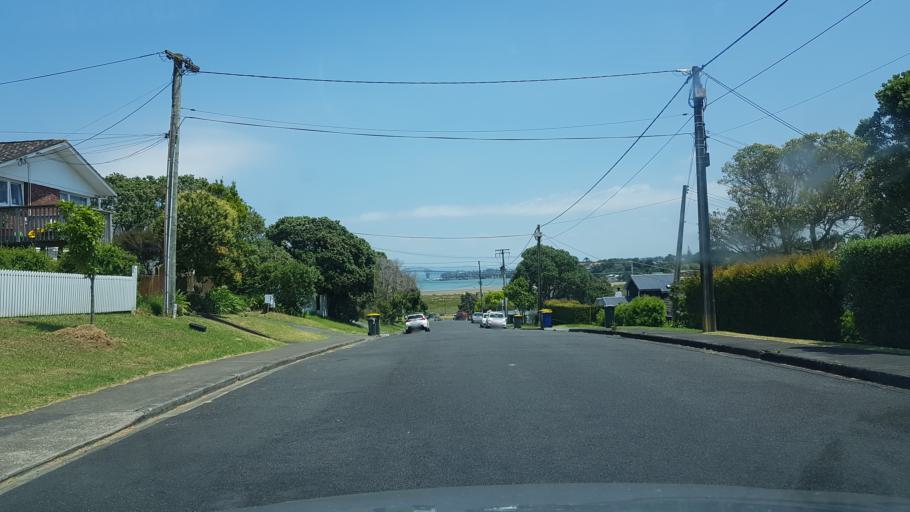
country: NZ
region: Auckland
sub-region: Auckland
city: North Shore
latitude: -36.8145
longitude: 174.7897
